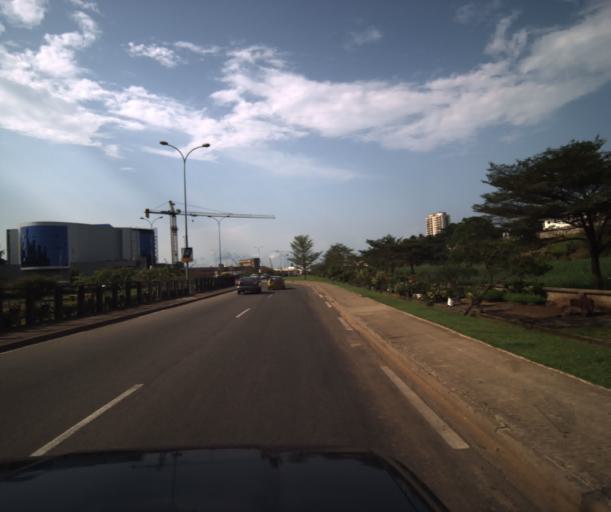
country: CM
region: Littoral
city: Douala
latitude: 4.0455
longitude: 9.6906
